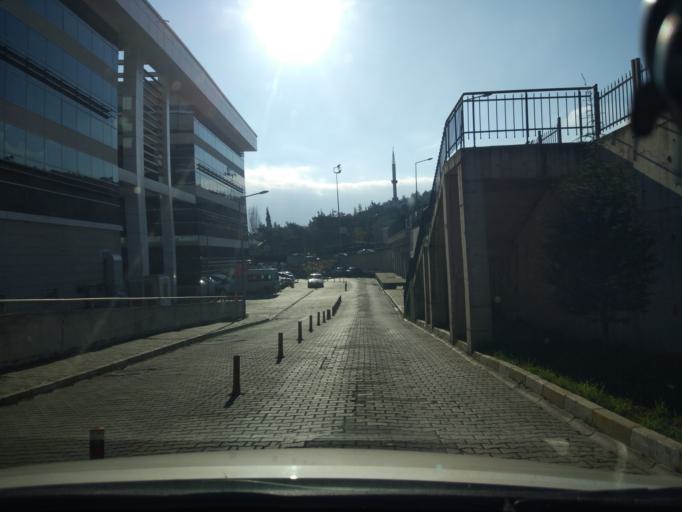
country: TR
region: Karabuk
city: Karabuk
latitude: 41.2097
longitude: 32.6184
